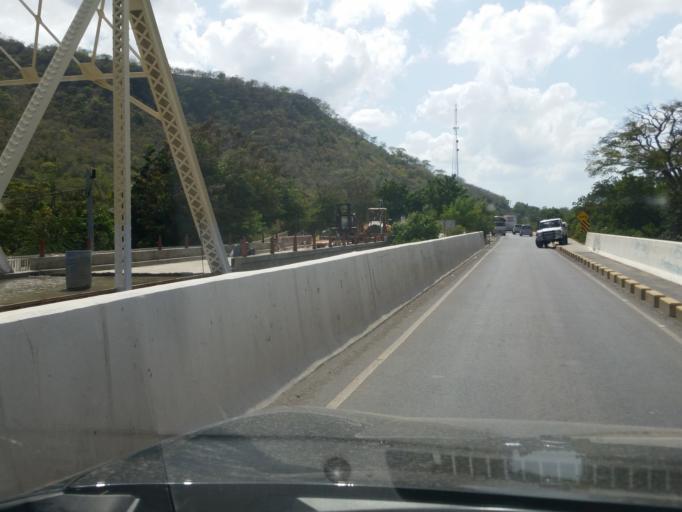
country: NI
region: Boaco
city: San Lorenzo
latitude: 12.2523
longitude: -85.6439
